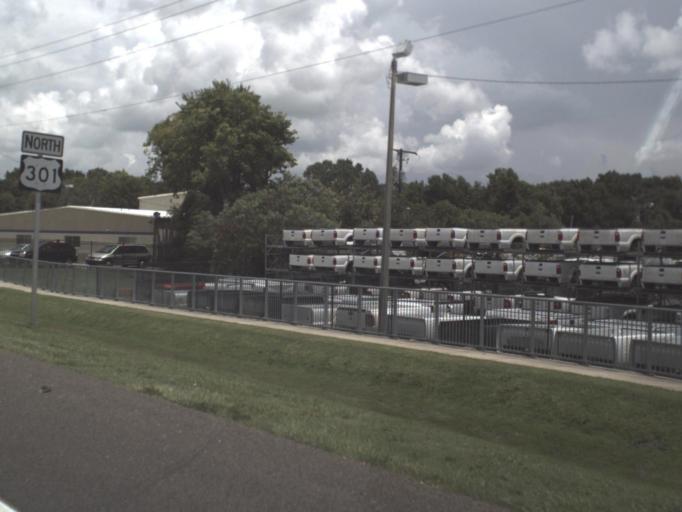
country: US
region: Florida
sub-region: Hillsborough County
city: Temple Terrace
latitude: 28.0228
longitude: -82.3502
